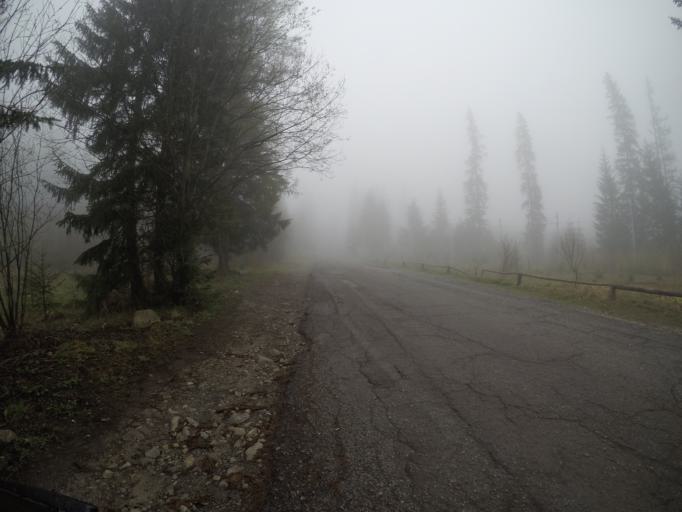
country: SK
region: Presovsky
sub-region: Okres Poprad
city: Strba
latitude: 49.1266
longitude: 20.0746
